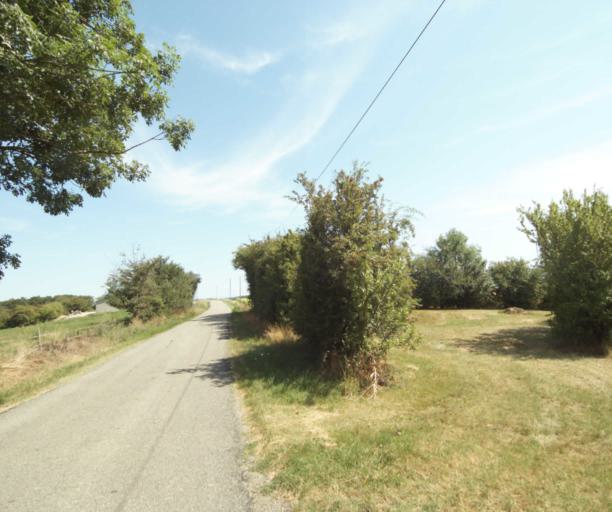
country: FR
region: Midi-Pyrenees
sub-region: Departement de la Haute-Garonne
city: Gaillac-Toulza
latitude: 43.2466
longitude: 1.4211
